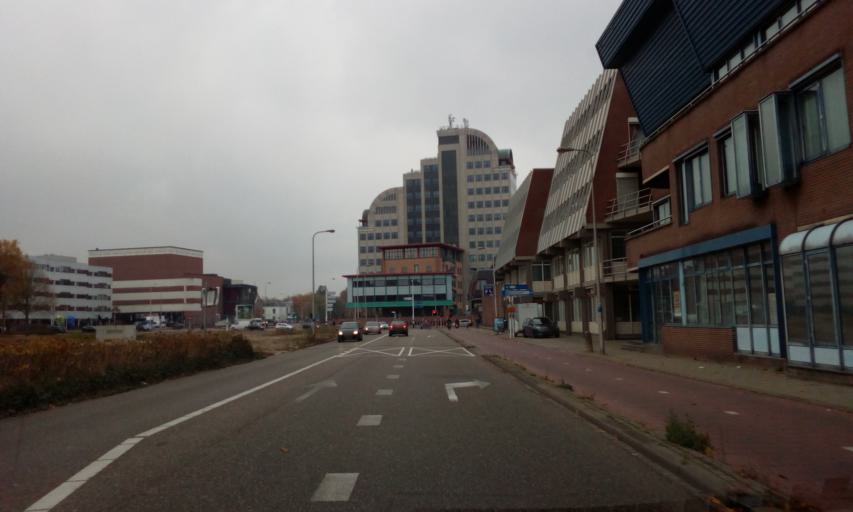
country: NL
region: Overijssel
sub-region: Gemeente Deventer
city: Deventer
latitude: 52.2549
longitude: 6.1652
